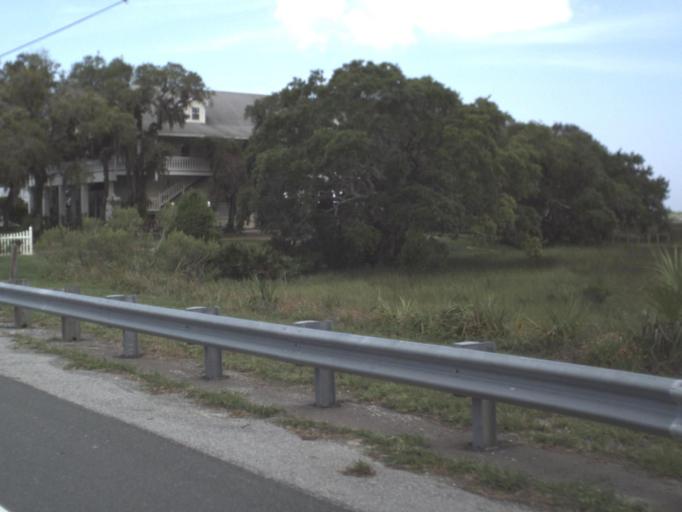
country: US
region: Florida
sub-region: Levy County
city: Chiefland
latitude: 29.1635
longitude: -83.0280
